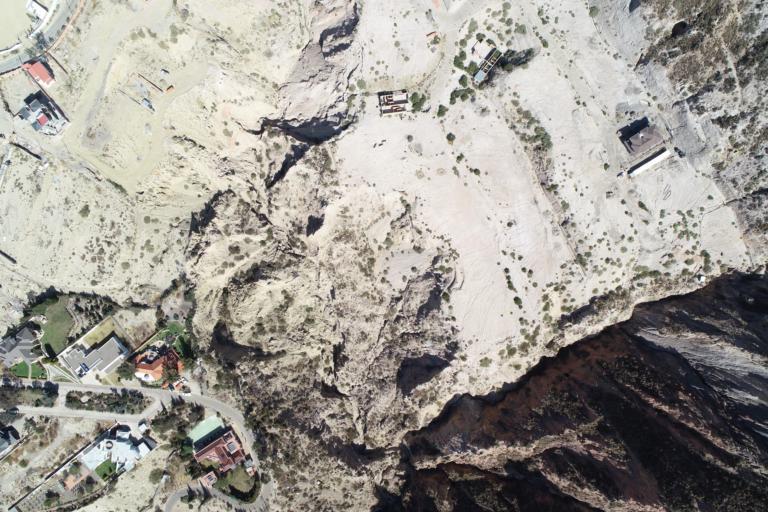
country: BO
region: La Paz
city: La Paz
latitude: -16.5565
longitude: -68.1058
